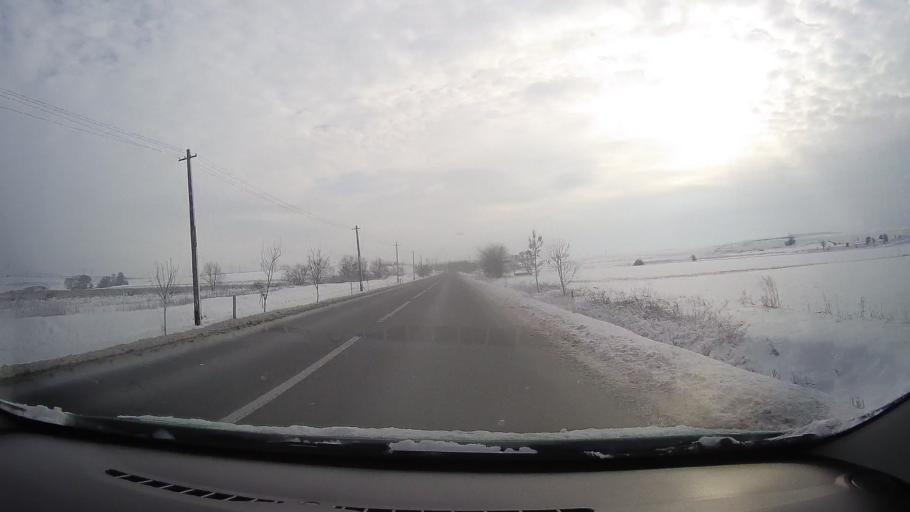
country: RO
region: Alba
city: Vurpar
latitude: 45.9873
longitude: 23.5085
